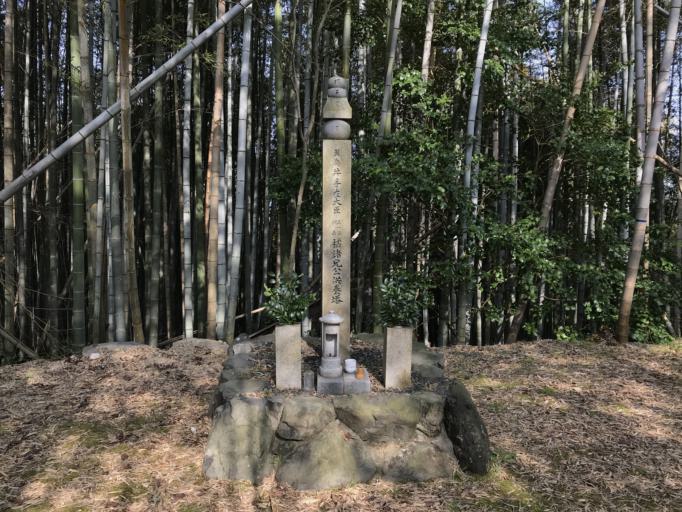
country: JP
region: Kyoto
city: Tanabe
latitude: 34.7970
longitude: 135.8188
